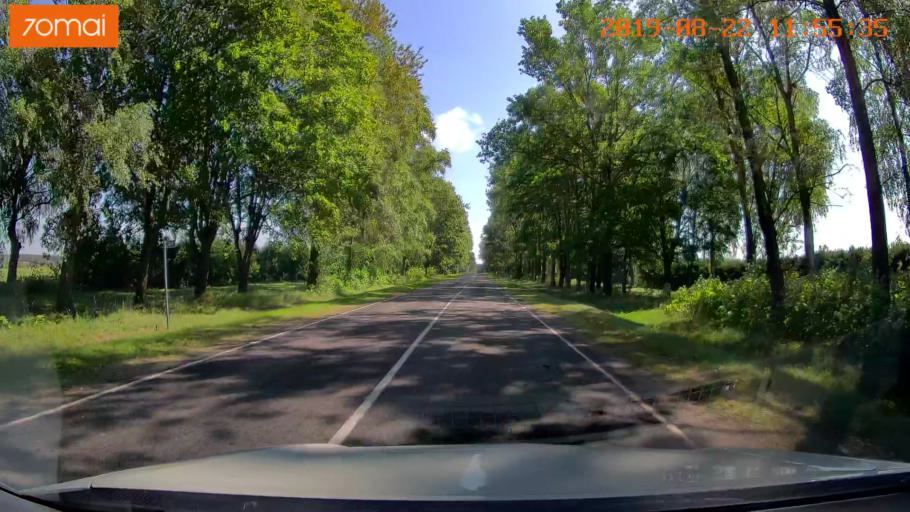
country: BY
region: Minsk
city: Prawdzinski
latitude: 53.4311
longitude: 27.5510
